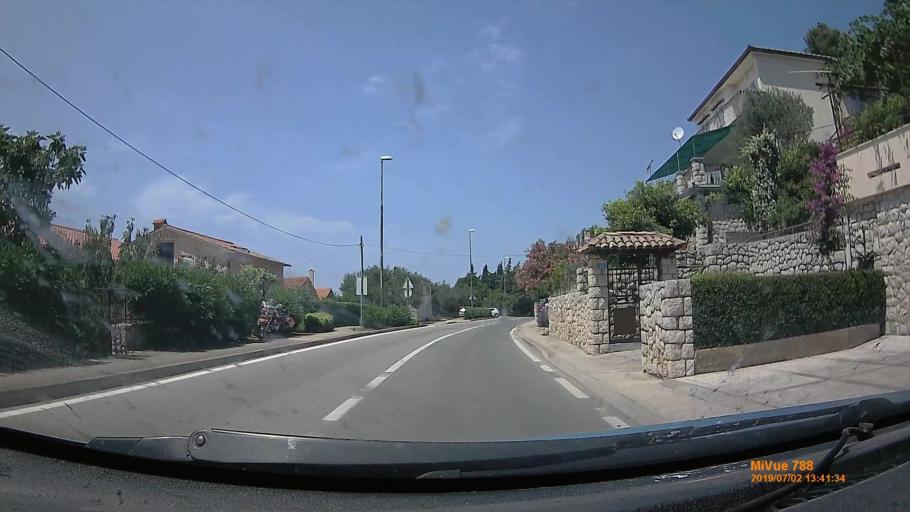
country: HR
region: Primorsko-Goranska
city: Mali Losinj
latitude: 44.5374
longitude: 14.4675
